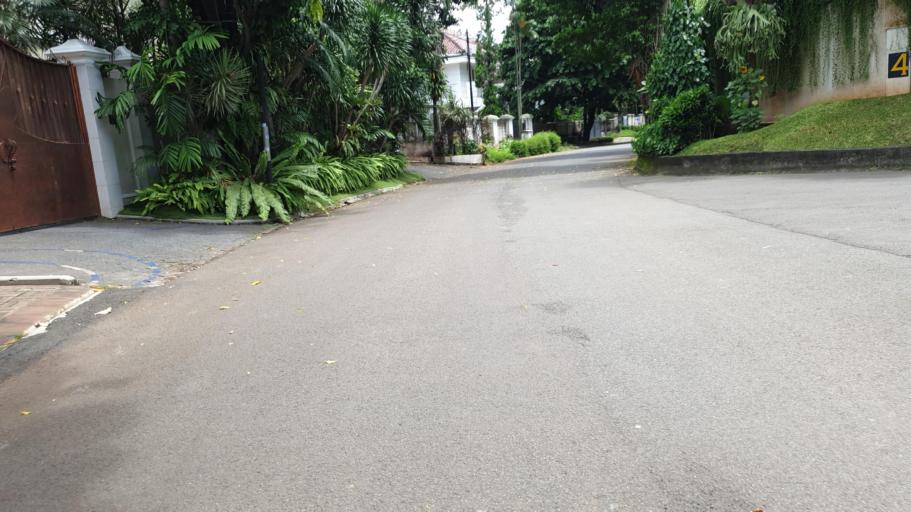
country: ID
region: Banten
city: South Tangerang
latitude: -6.2781
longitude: 106.7865
